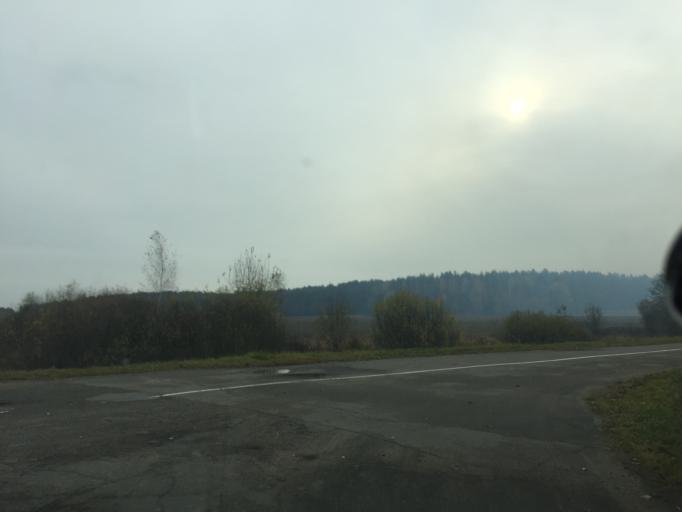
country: BY
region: Mogilev
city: Drybin
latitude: 54.0142
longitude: 31.0213
